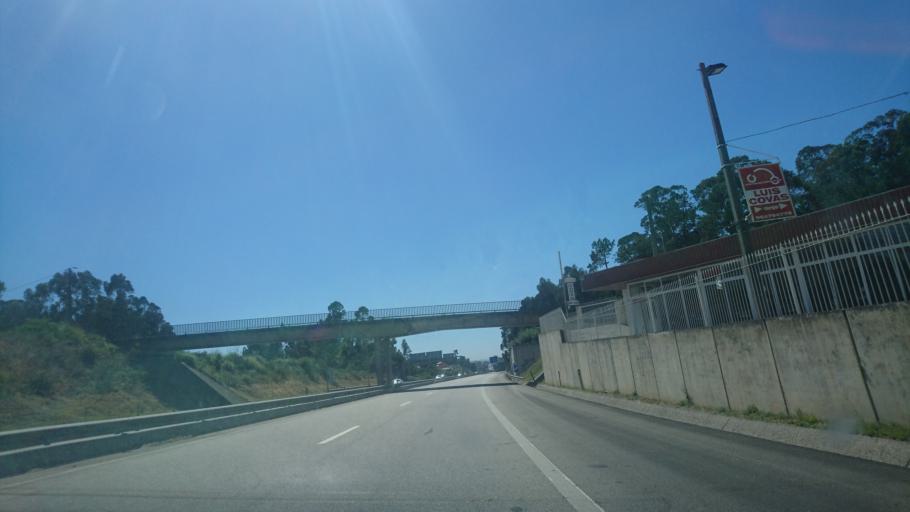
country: PT
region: Aveiro
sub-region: Santa Maria da Feira
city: Nogueira da Regedoura
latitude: 41.0085
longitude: -8.5996
